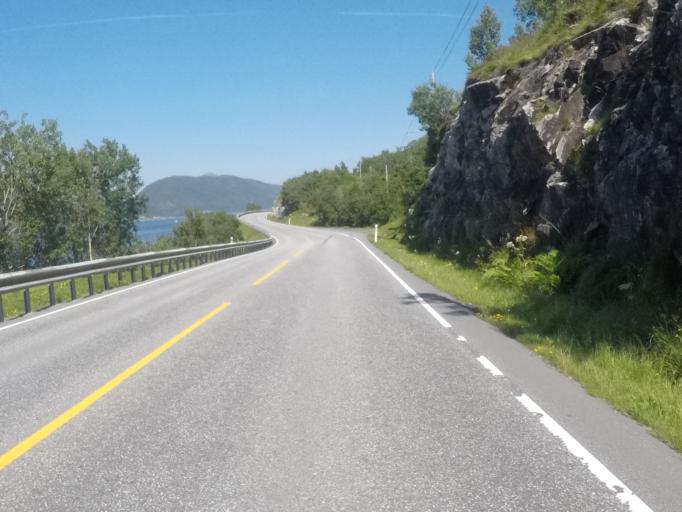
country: NO
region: More og Romsdal
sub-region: Hareid
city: Hareid
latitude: 62.2627
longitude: 5.9779
